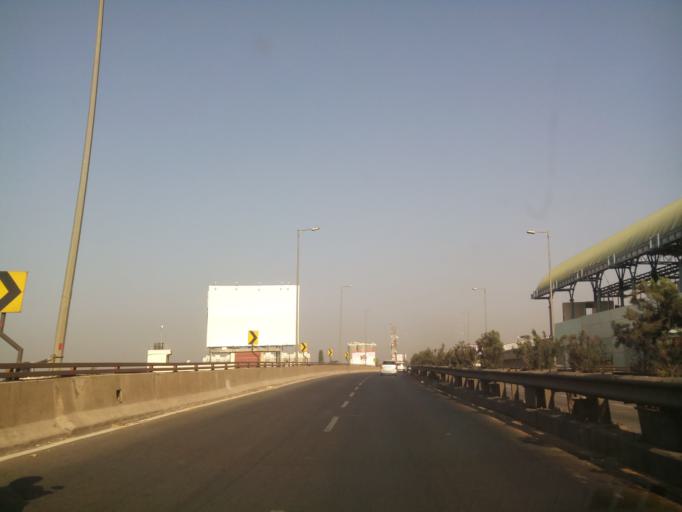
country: IN
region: Karnataka
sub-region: Bangalore Urban
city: Yelahanka
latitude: 13.0431
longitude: 77.5124
